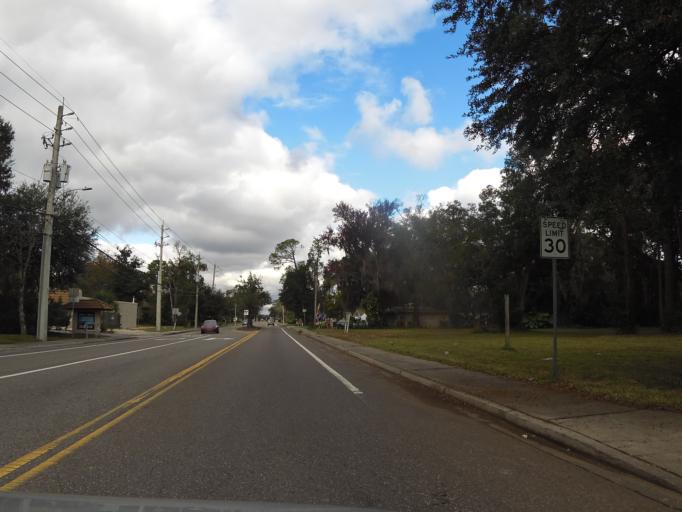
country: US
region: Florida
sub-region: Duval County
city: Jacksonville
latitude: 30.2652
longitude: -81.6075
